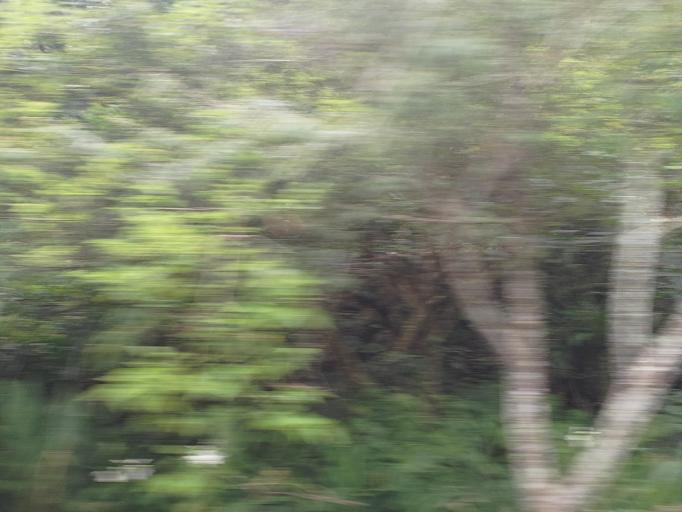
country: TW
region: Taiwan
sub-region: Hsinchu
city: Hsinchu
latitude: 24.6134
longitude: 121.0413
